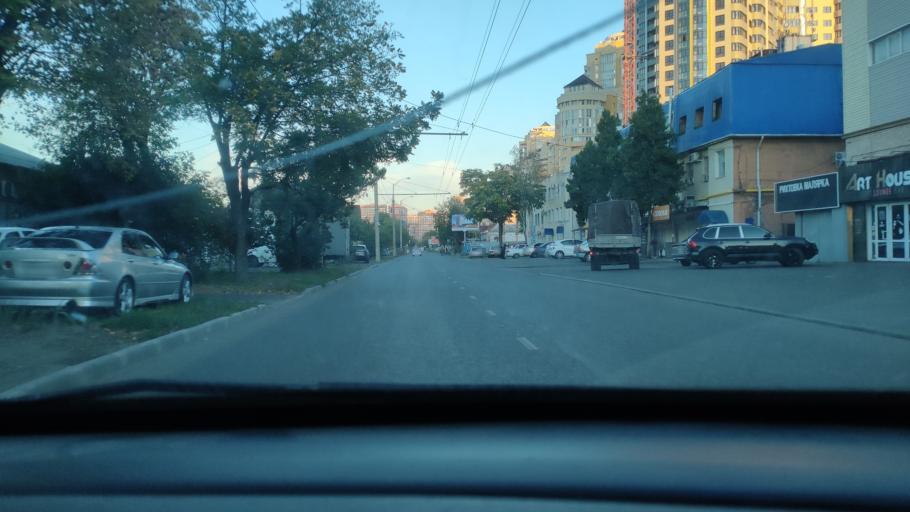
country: RU
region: Krasnodarskiy
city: Krasnodar
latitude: 45.0383
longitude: 38.9383
